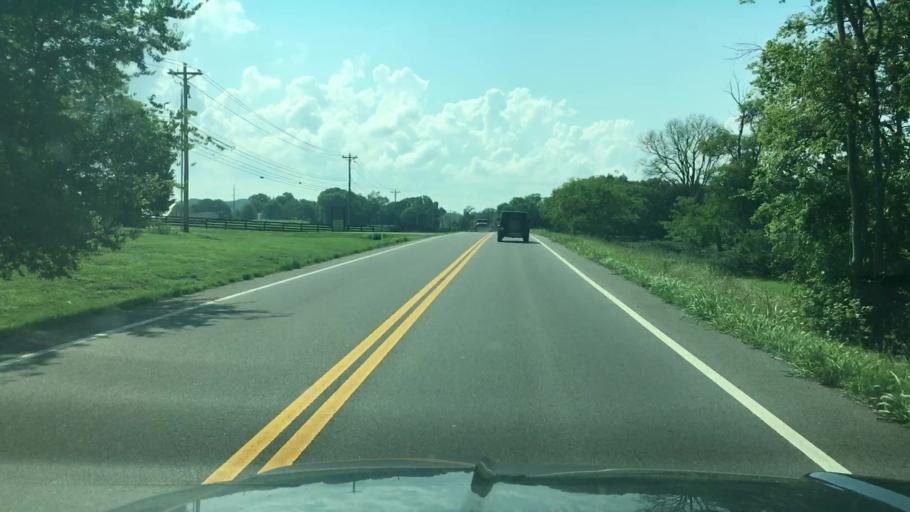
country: US
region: Tennessee
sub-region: Williamson County
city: Nolensville
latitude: 35.8804
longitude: -86.7441
